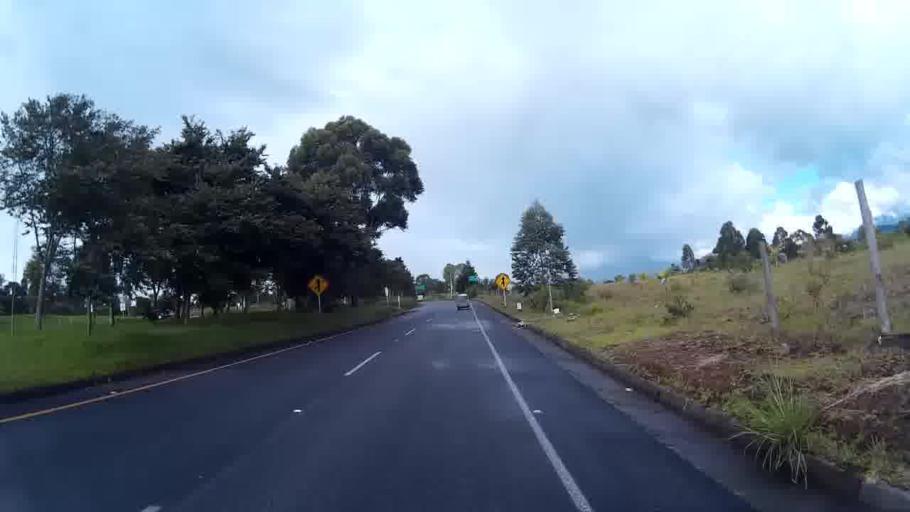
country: CO
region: Quindio
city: Circasia
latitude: 4.6359
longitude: -75.6132
